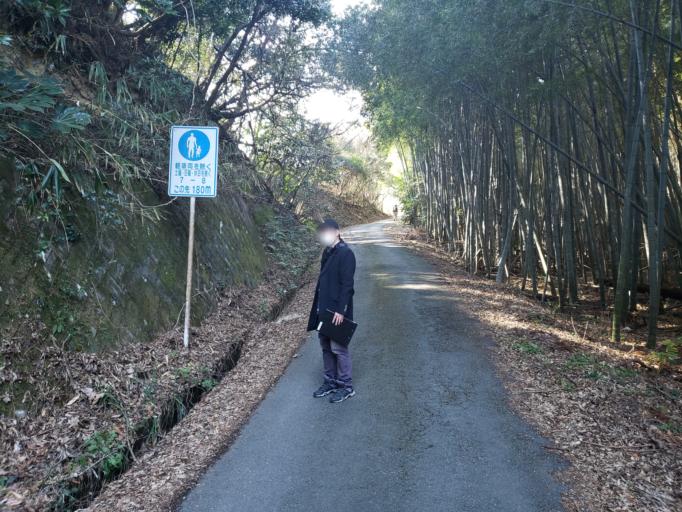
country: JP
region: Shizuoka
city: Kosai-shi
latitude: 34.6814
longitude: 137.5134
